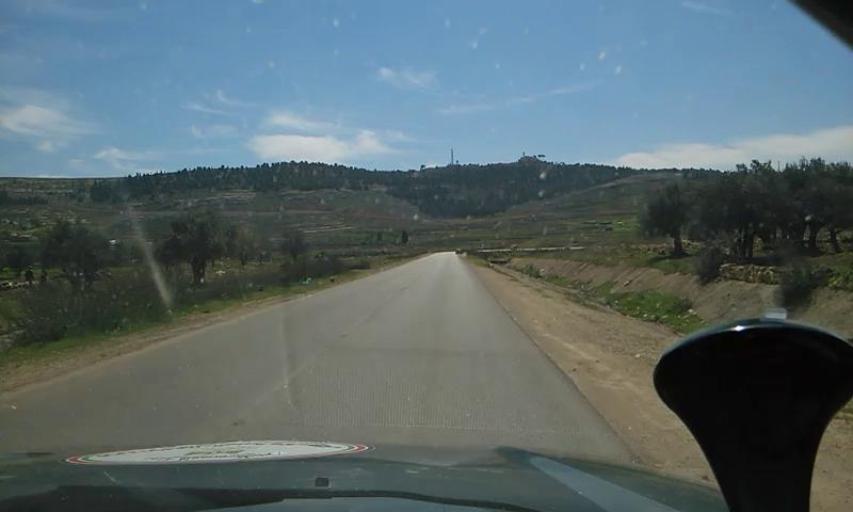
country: PS
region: West Bank
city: Al Jib
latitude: 31.8449
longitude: 35.1807
